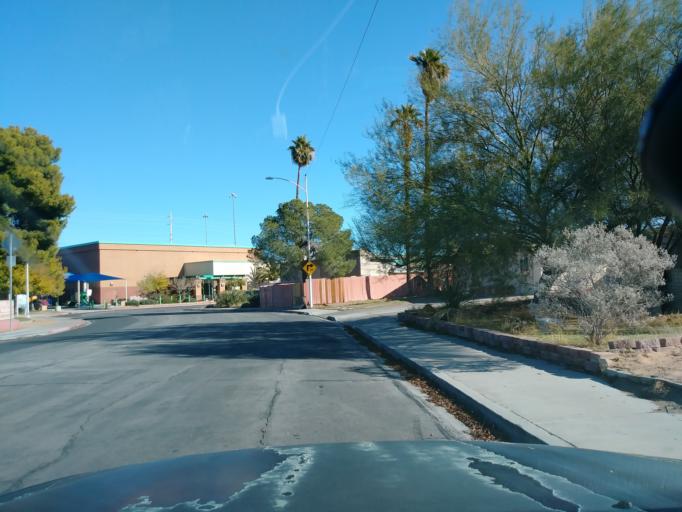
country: US
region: Nevada
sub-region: Clark County
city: Spring Valley
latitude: 36.1725
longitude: -115.2282
